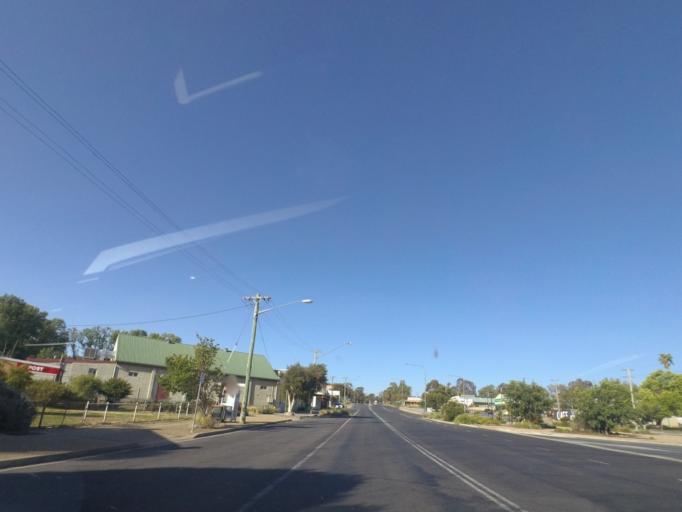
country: AU
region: New South Wales
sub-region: Wagga Wagga
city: Forest Hill
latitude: -35.2771
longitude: 147.7368
